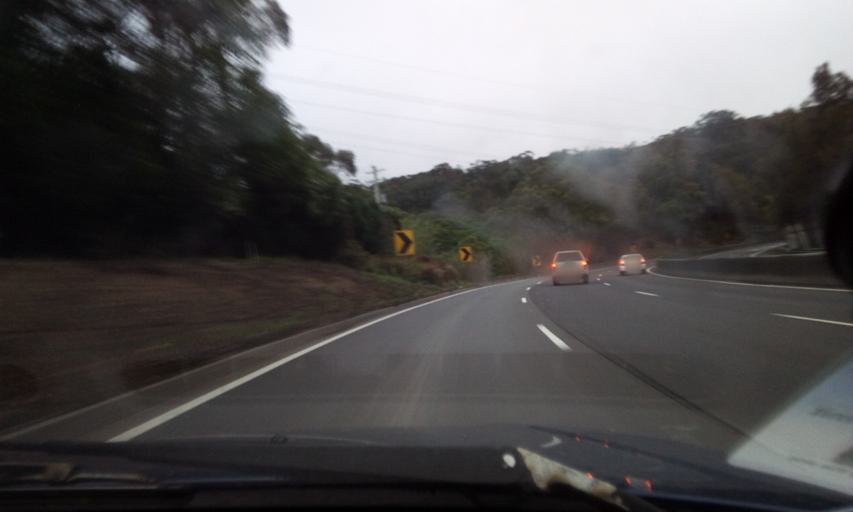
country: AU
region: New South Wales
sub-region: Wollongong
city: Mount Ousley
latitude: -34.4013
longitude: 150.8701
